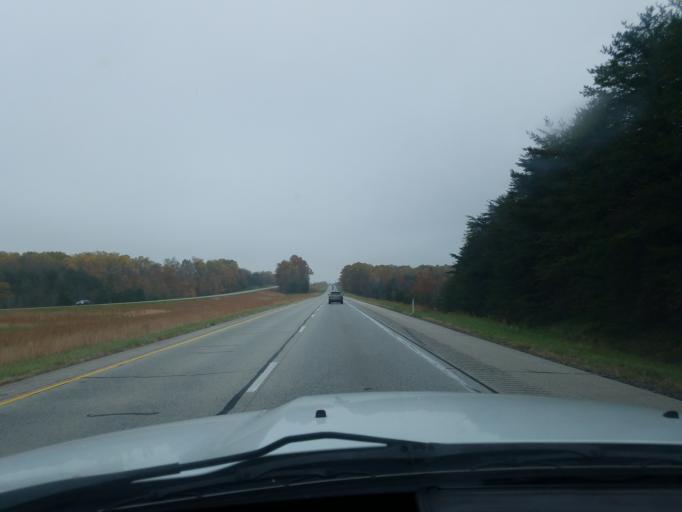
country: US
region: Indiana
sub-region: Floyd County
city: Georgetown
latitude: 38.2541
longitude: -86.0319
